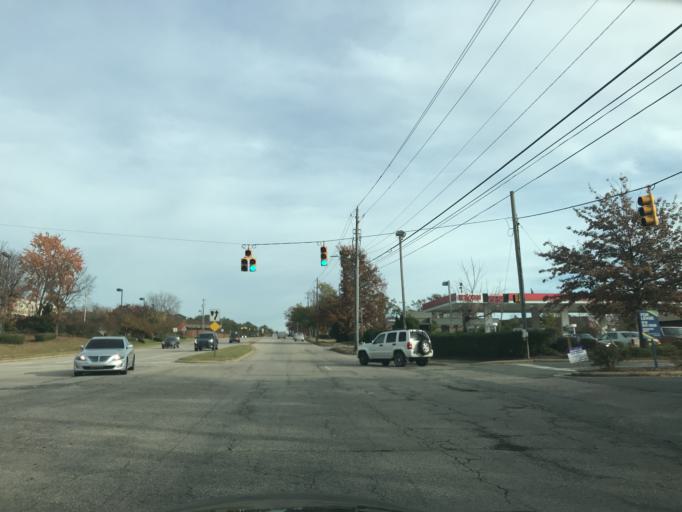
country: US
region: North Carolina
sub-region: Wake County
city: West Raleigh
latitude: 35.9015
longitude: -78.6557
